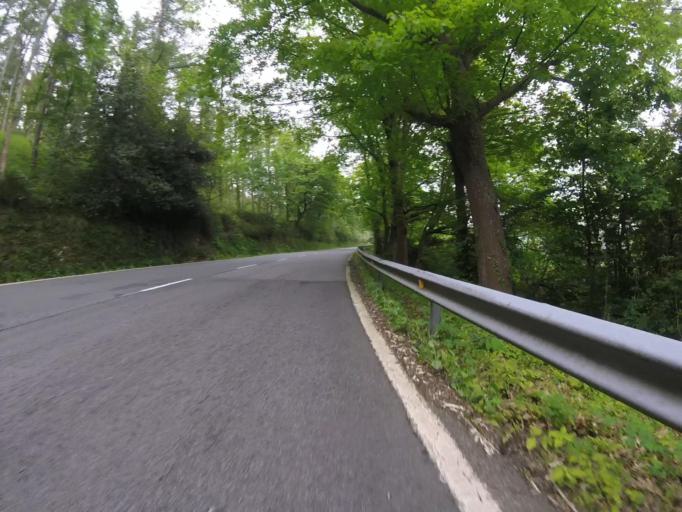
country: ES
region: Navarre
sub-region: Provincia de Navarra
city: Zugarramurdi
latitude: 43.2620
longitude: -1.4887
